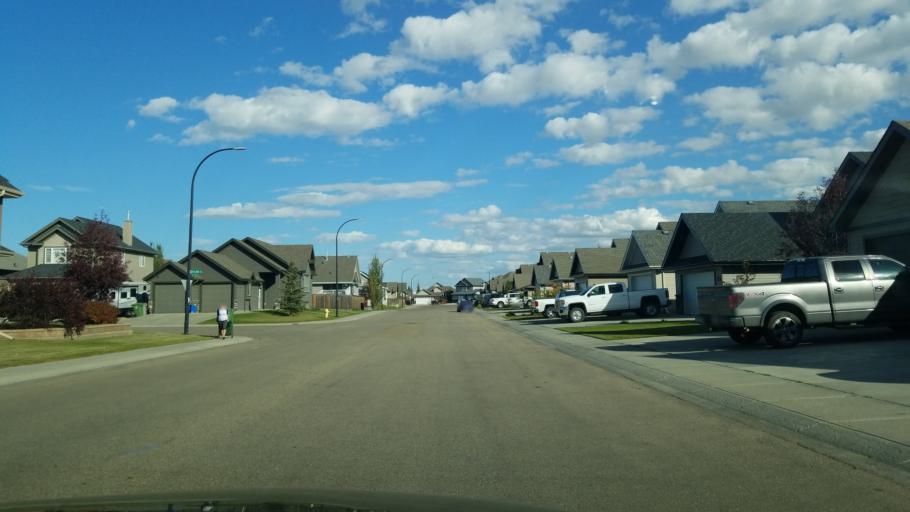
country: CA
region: Saskatchewan
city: Lloydminster
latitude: 53.2522
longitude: -110.0192
